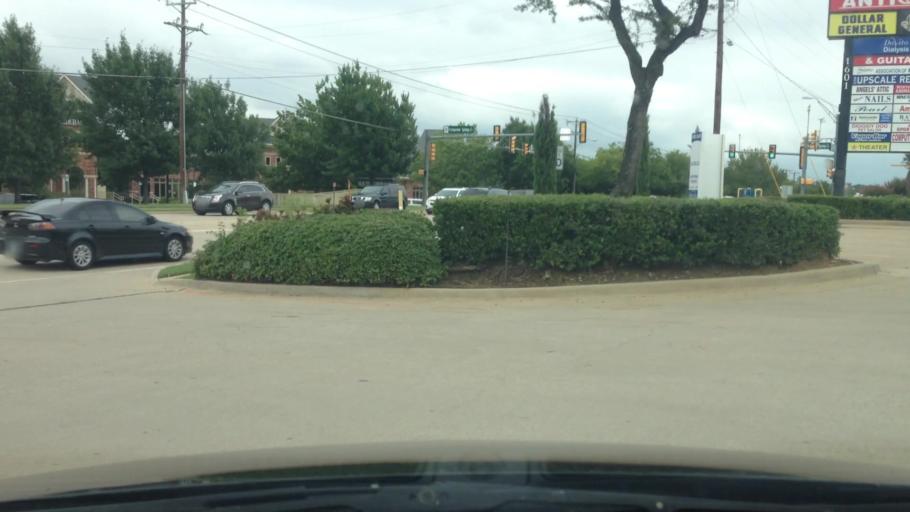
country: US
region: Texas
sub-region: Tarrant County
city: Grapevine
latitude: 32.9409
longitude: -97.0940
